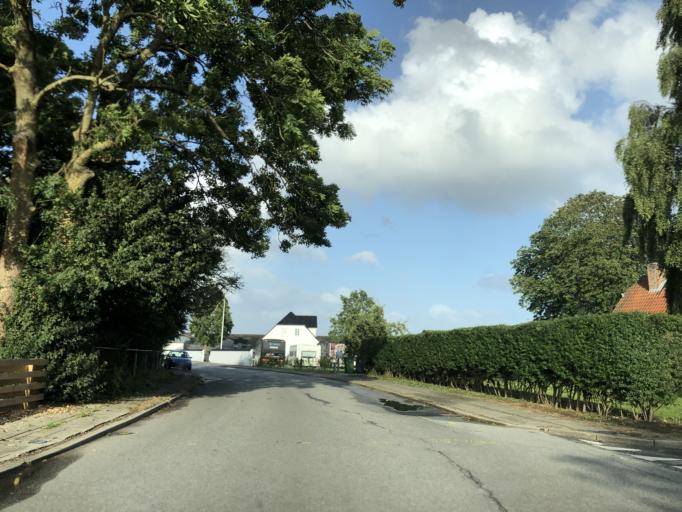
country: DK
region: South Denmark
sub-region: Haderslev Kommune
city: Starup
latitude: 55.1924
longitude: 9.5192
